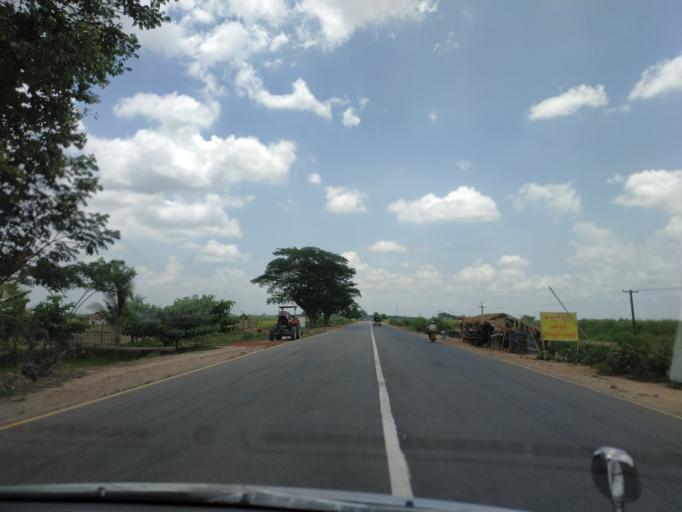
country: MM
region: Bago
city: Bago
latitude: 17.4698
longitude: 96.5603
